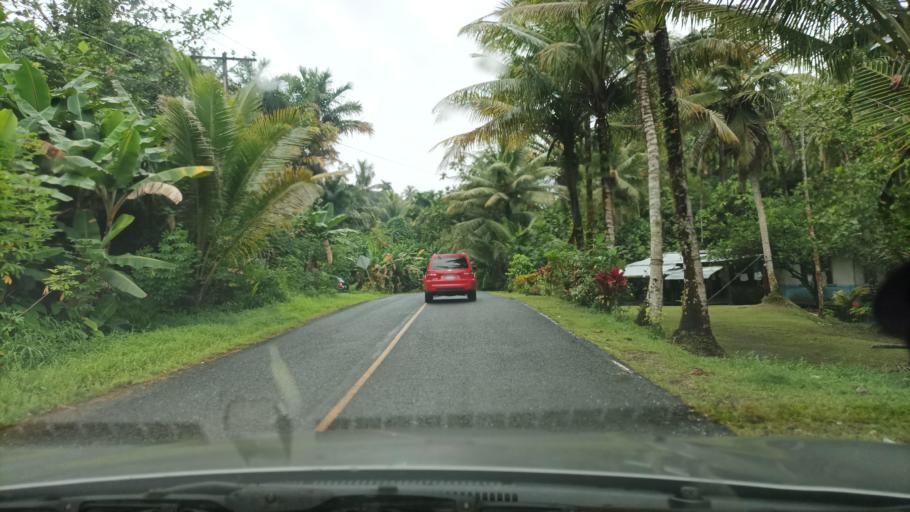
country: FM
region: Pohnpei
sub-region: Madolenihm Municipality
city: Madolenihm Municipality Government
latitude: 6.8088
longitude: 158.2591
